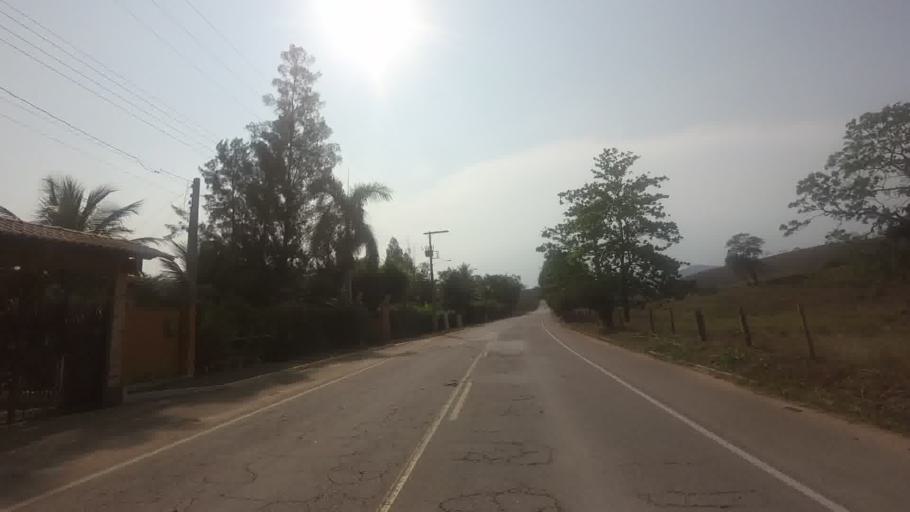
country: BR
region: Rio de Janeiro
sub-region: Bom Jesus Do Itabapoana
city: Bom Jesus do Itabapoana
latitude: -21.1446
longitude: -41.6259
